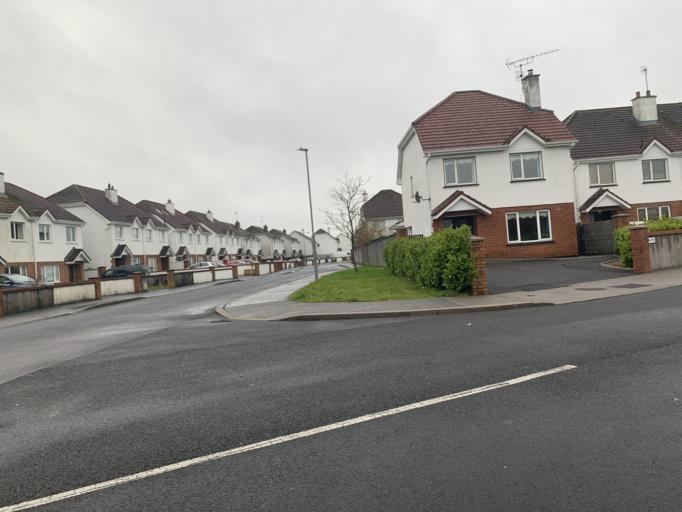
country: IE
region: Connaught
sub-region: County Galway
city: Tuam
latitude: 53.5115
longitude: -8.8727
